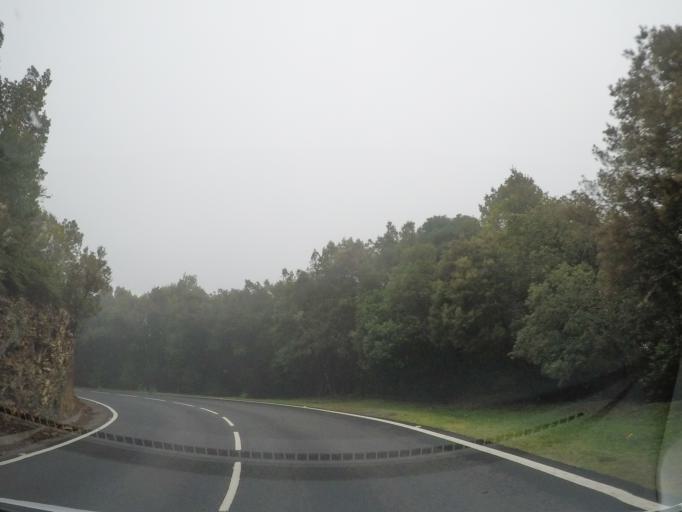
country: ES
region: Canary Islands
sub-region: Provincia de Santa Cruz de Tenerife
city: Vallehermosa
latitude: 28.1257
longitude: -17.2562
